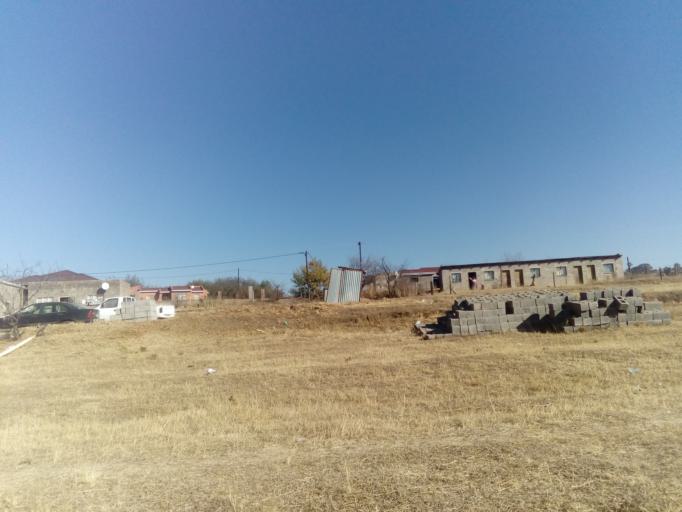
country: LS
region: Berea
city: Teyateyaneng
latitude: -29.1435
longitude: 27.7645
